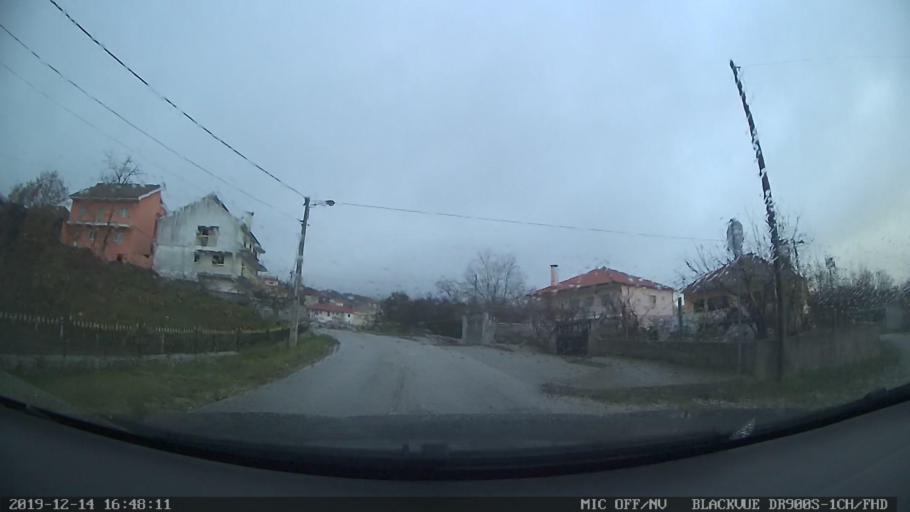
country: PT
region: Vila Real
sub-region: Murca
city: Murca
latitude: 41.4044
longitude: -7.5005
